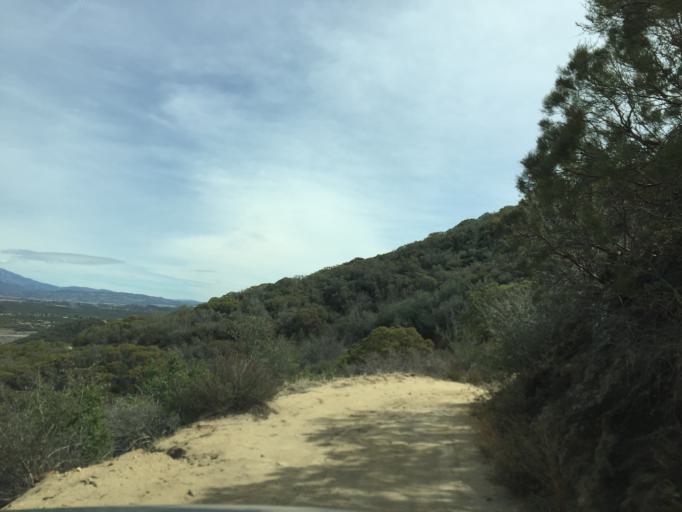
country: US
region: California
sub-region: Riverside County
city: Anza
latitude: 33.5938
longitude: -116.7764
